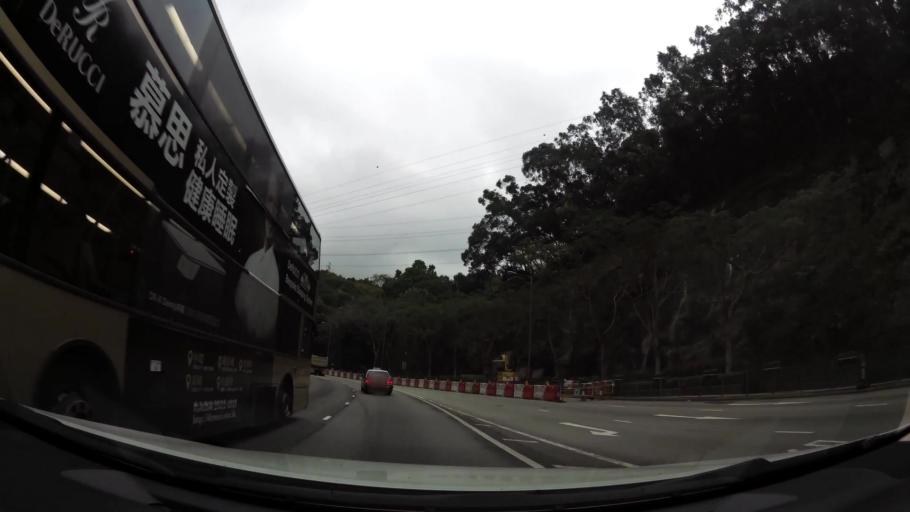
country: HK
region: Tsuen Wan
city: Tsuen Wan
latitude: 22.3788
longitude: 114.1372
